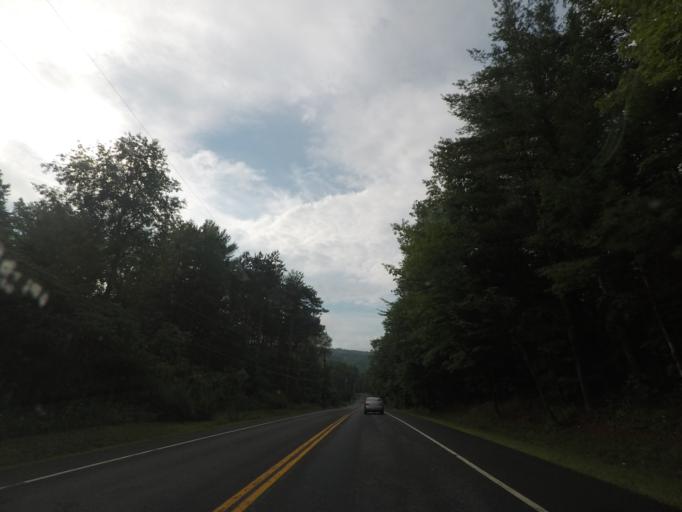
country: US
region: New York
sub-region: Rensselaer County
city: Nassau
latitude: 42.4988
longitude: -73.5554
